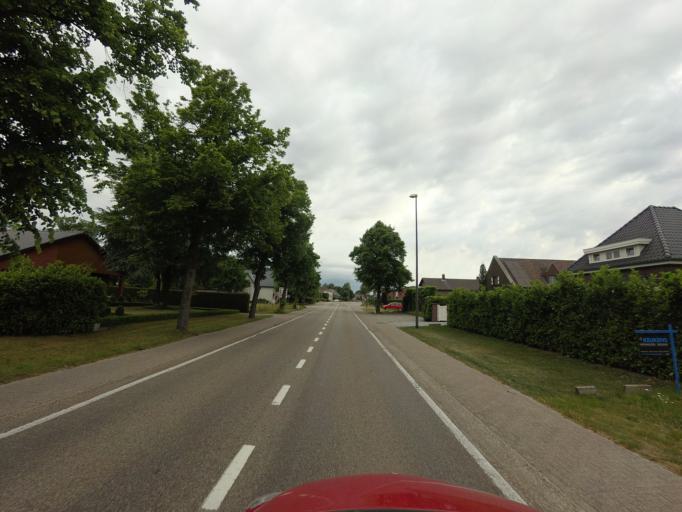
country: BE
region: Flanders
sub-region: Provincie Limburg
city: Lommel
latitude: 51.2046
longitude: 5.3079
